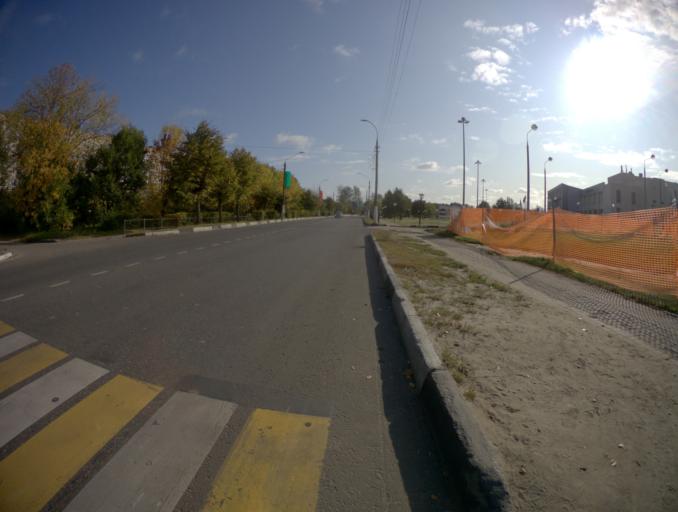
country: RU
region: Moskovskaya
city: Roshal'
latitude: 55.6634
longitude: 39.8605
